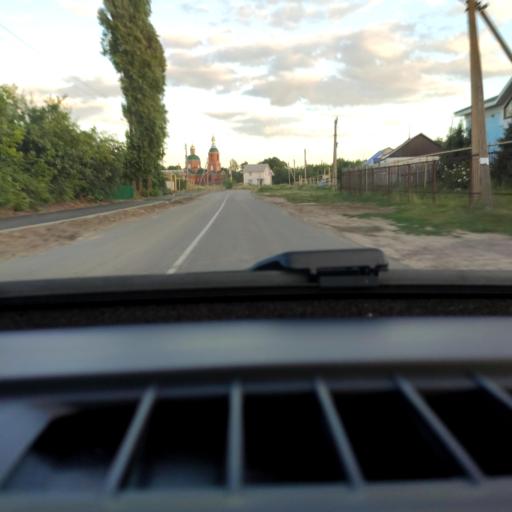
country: RU
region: Voronezj
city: Orlovo
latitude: 51.6562
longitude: 39.7031
